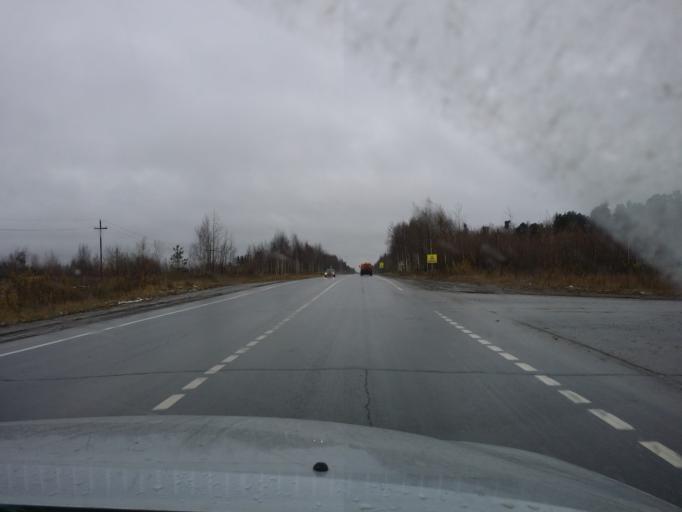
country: RU
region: Khanty-Mansiyskiy Avtonomnyy Okrug
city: Megion
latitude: 61.0611
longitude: 76.1151
